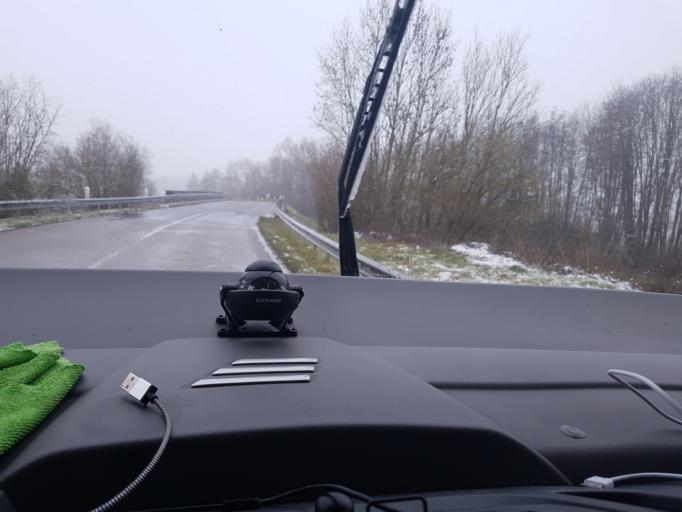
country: FR
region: Lorraine
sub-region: Departement de la Moselle
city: Dieuze
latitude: 48.6844
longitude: 6.7797
